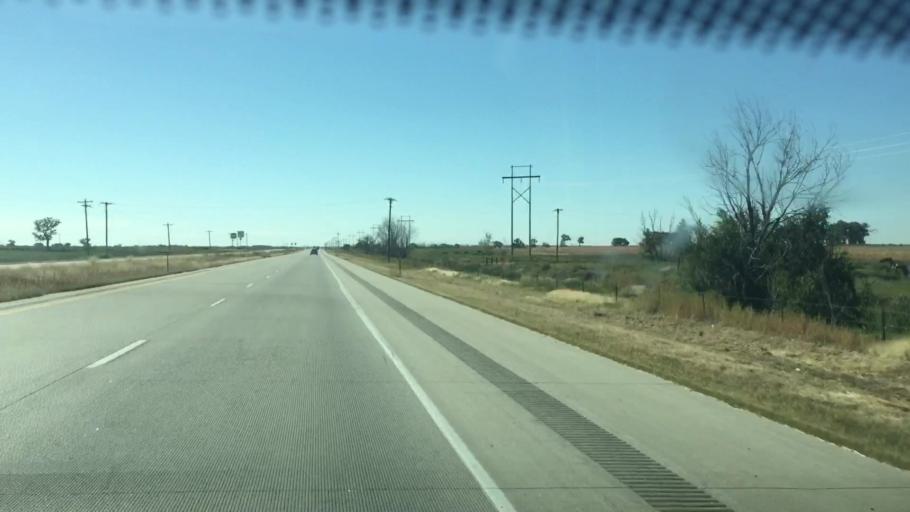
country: US
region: Colorado
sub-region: Prowers County
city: Lamar
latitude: 38.1102
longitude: -102.6763
